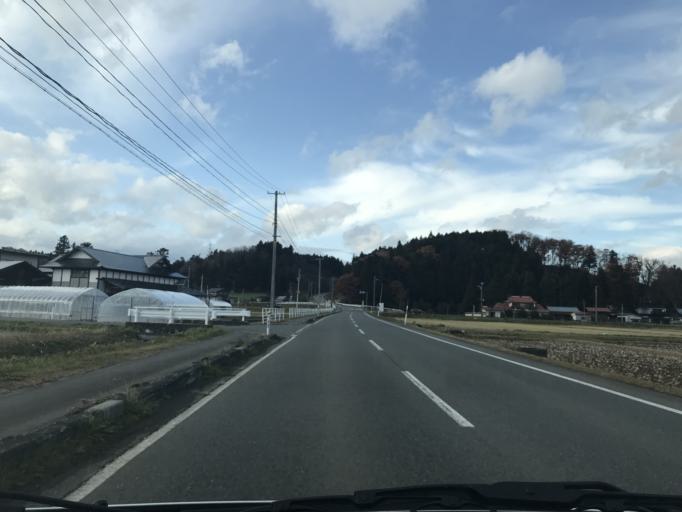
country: JP
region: Iwate
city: Mizusawa
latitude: 39.1678
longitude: 141.0880
